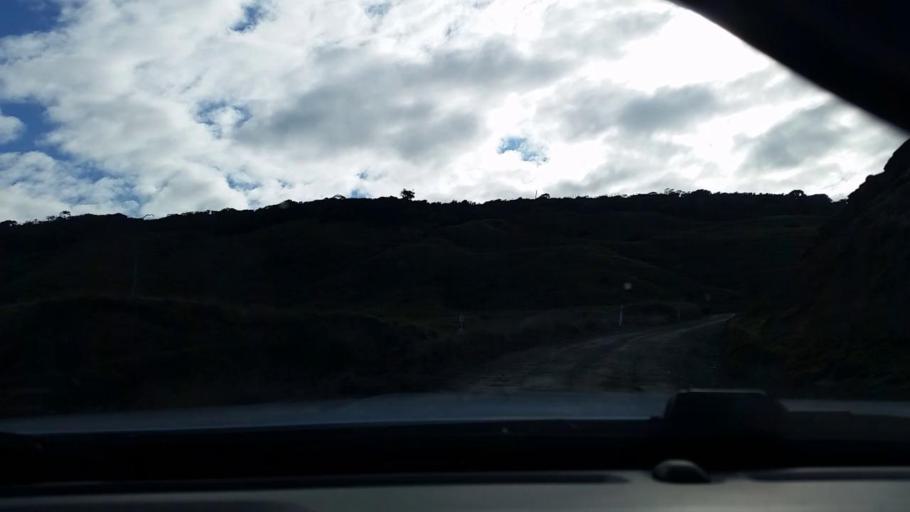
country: NZ
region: Southland
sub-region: Southland District
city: Riverton
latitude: -46.3312
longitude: 167.7126
